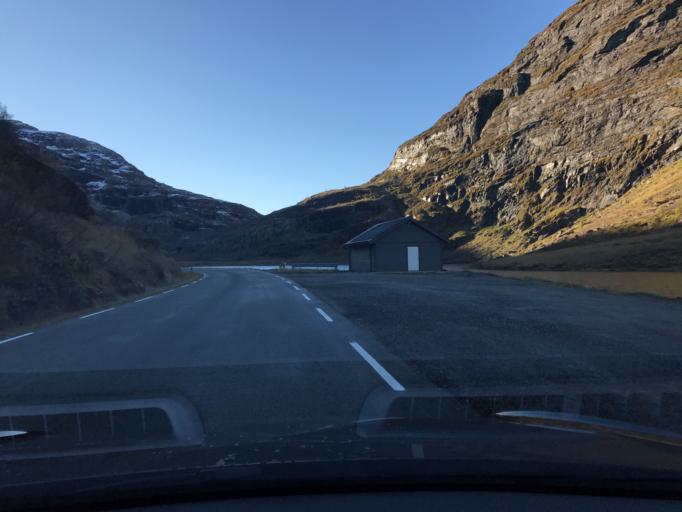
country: NO
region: Sogn og Fjordane
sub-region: Laerdal
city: Laerdalsoyri
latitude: 60.8080
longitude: 7.5590
